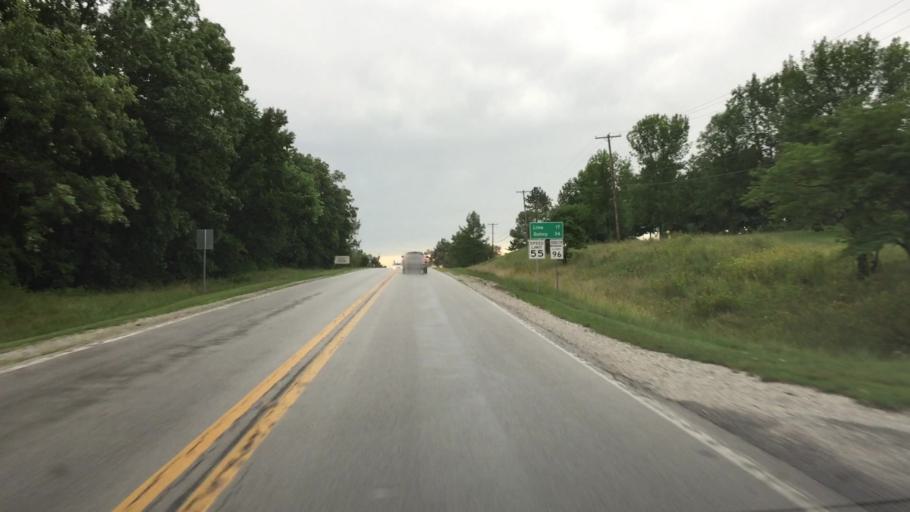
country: US
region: Illinois
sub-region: Hancock County
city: Hamilton
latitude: 40.3839
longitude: -91.3409
